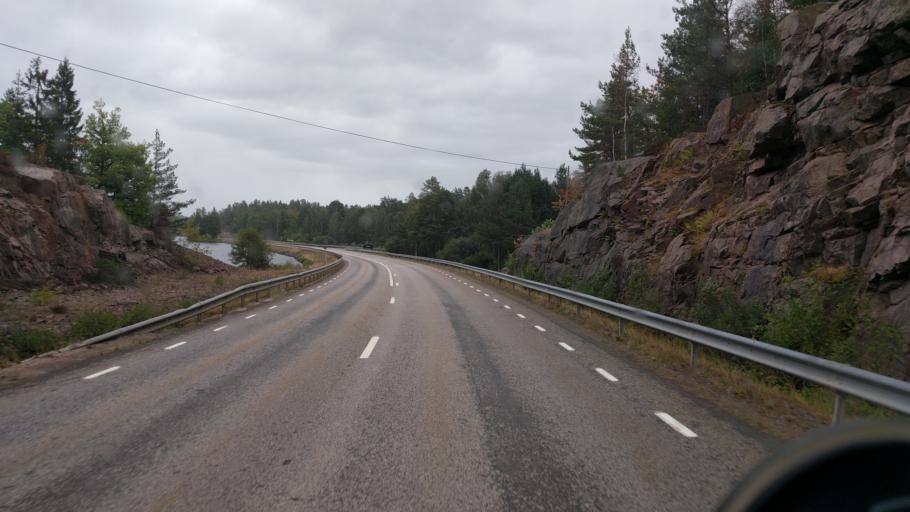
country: SE
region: Kalmar
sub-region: Vasterviks Kommun
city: Ankarsrum
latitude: 57.6961
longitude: 16.2861
